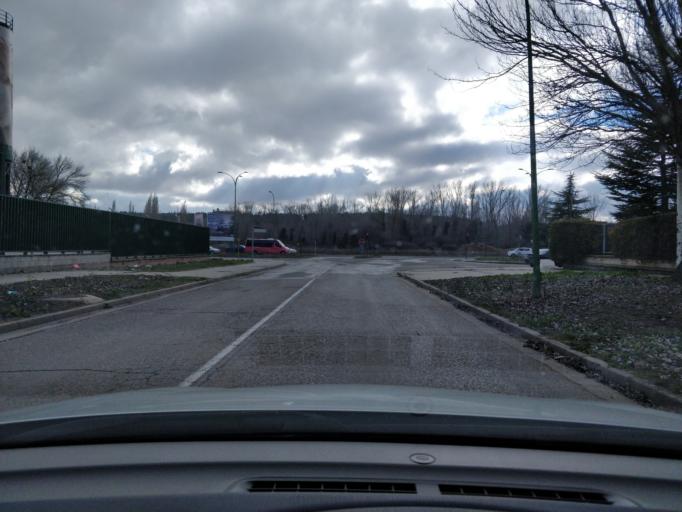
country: ES
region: Castille and Leon
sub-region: Provincia de Burgos
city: Burgos
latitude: 42.3469
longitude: -3.6584
